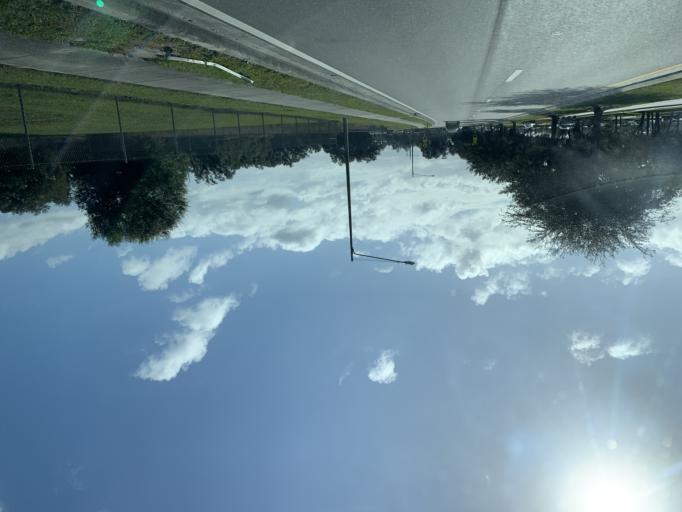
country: US
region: Florida
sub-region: Orange County
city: Clarcona
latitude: 28.6399
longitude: -81.4748
